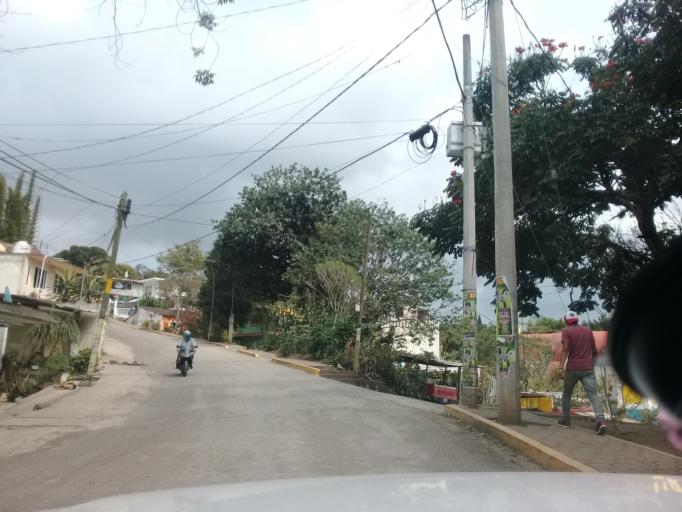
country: MX
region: Veracruz
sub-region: Xalapa
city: Fraccionamiento las Fuentes
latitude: 19.4754
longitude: -96.8789
